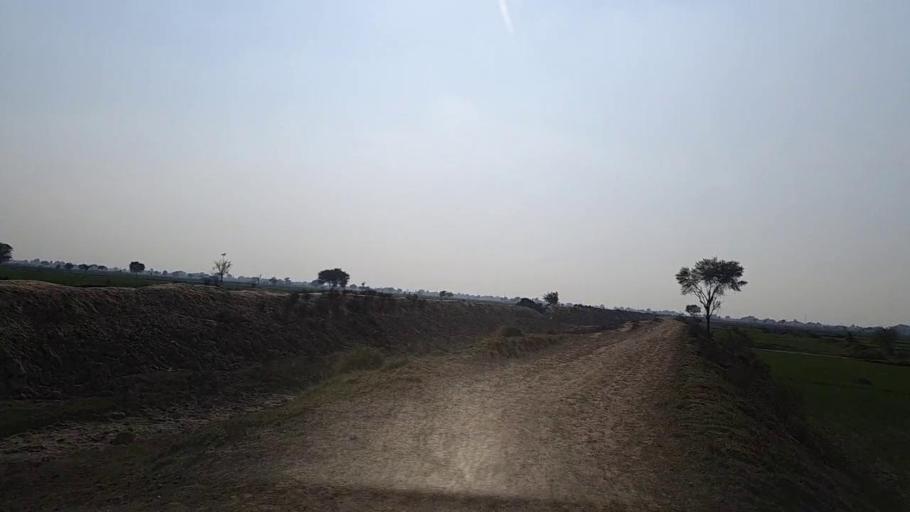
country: PK
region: Sindh
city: Moro
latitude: 26.7444
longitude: 67.9388
